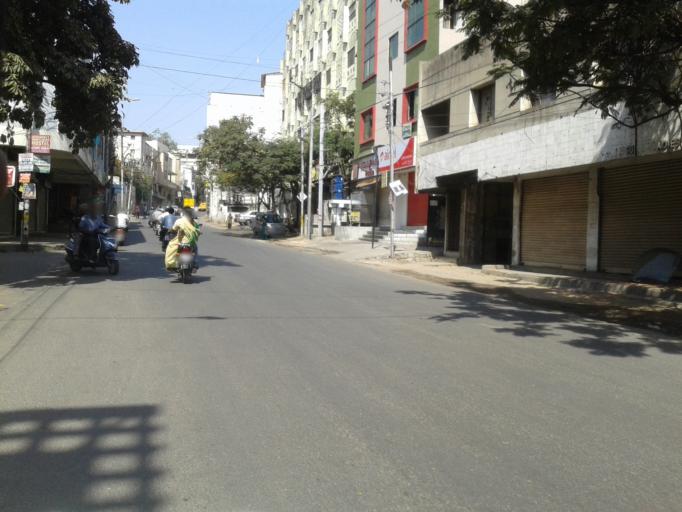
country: IN
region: Telangana
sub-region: Hyderabad
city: Hyderabad
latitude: 17.3945
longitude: 78.4800
